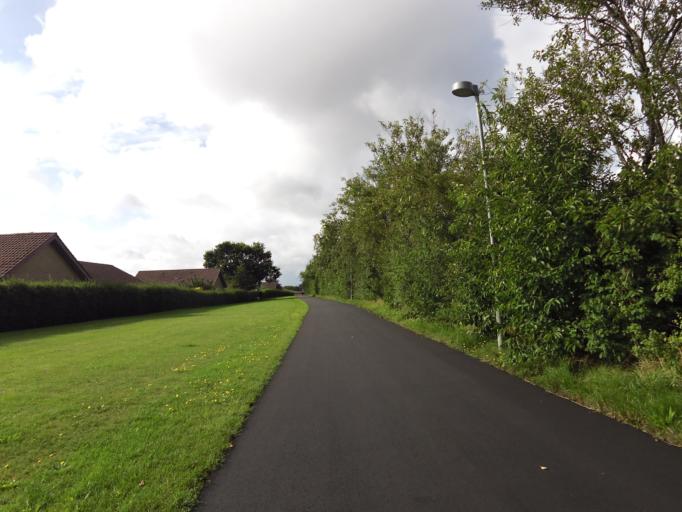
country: DK
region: South Denmark
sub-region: Esbjerg Kommune
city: Ribe
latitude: 55.3386
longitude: 8.7816
